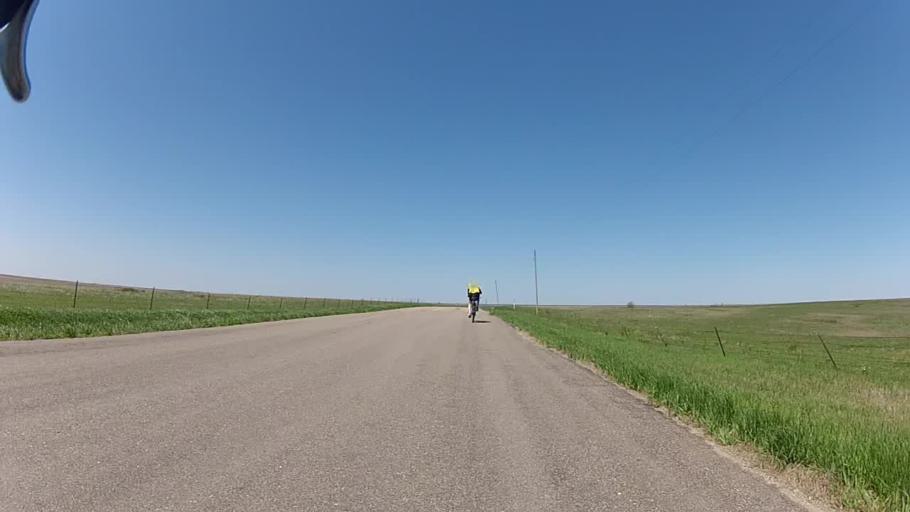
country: US
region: Kansas
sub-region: Riley County
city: Ogden
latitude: 38.9718
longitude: -96.5706
